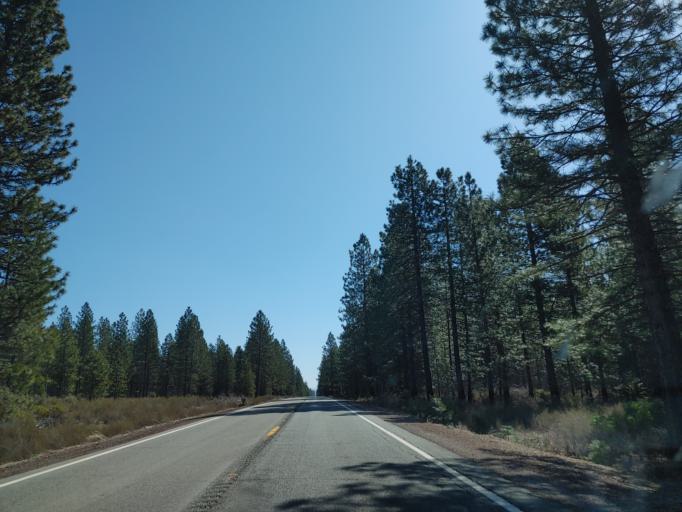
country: US
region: California
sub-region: Siskiyou County
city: McCloud
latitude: 41.2521
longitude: -122.1104
